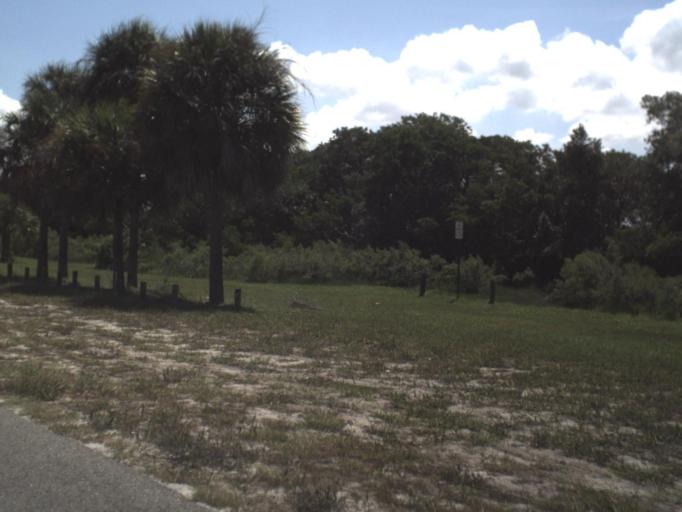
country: US
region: Florida
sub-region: Manatee County
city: Holmes Beach
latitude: 27.4972
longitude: -82.7033
